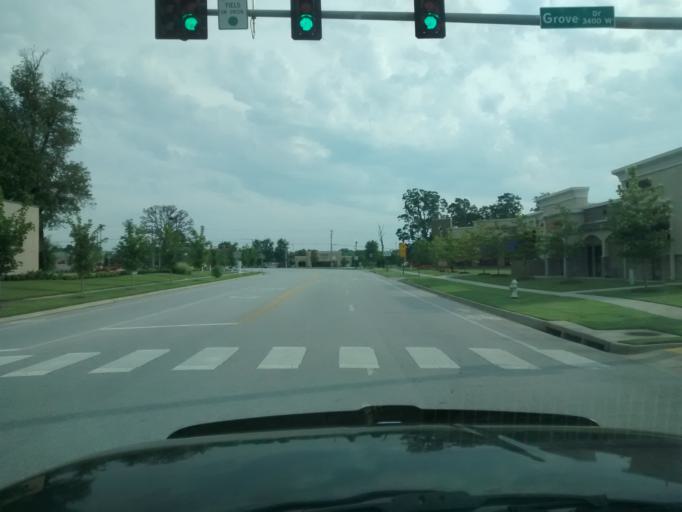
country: US
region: Arkansas
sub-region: Washington County
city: Farmington
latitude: 36.0764
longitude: -94.2087
